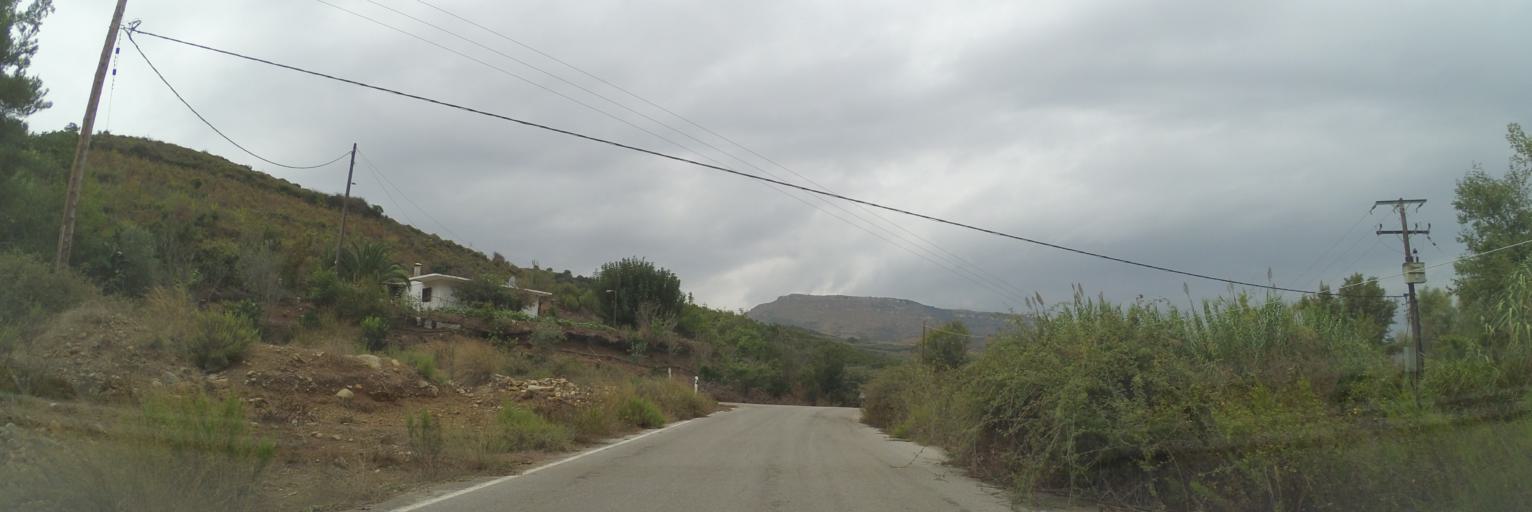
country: GR
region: Crete
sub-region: Nomos Rethymnis
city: Agia Foteini
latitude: 35.2875
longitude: 24.5658
